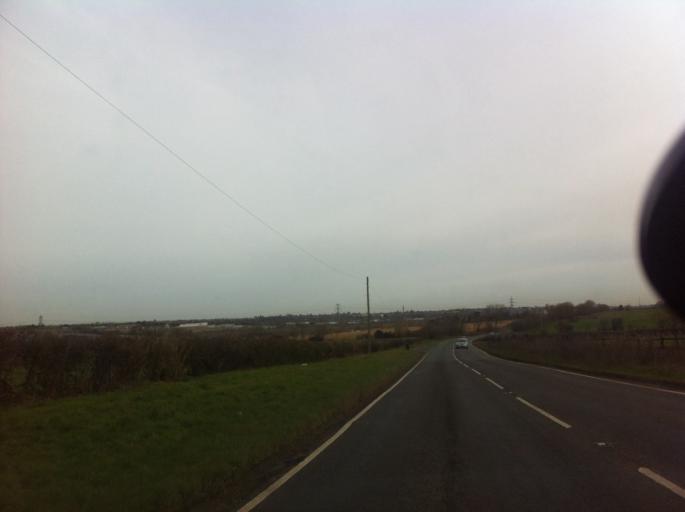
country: GB
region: England
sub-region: Northamptonshire
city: Irchester
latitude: 52.2711
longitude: -0.6760
